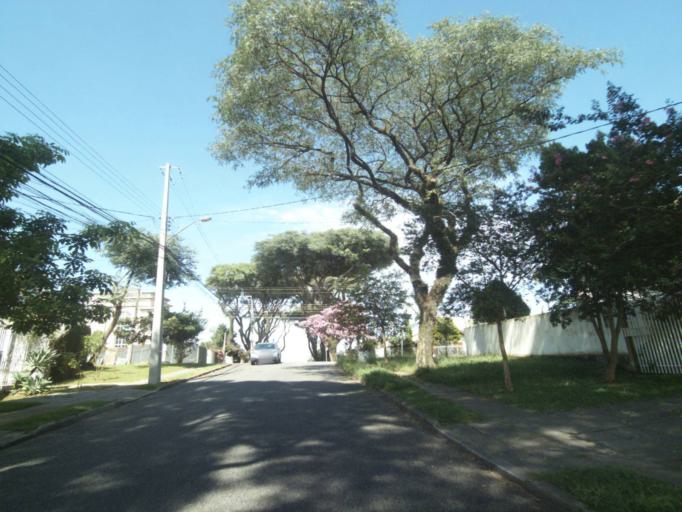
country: BR
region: Parana
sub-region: Curitiba
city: Curitiba
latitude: -25.4592
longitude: -49.2421
